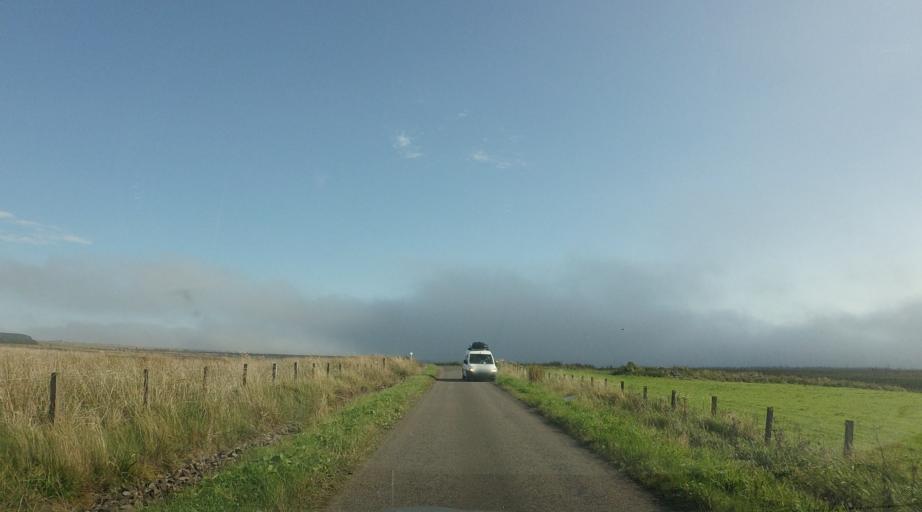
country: GB
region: Scotland
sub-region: Highland
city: Wick
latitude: 58.3347
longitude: -3.3363
